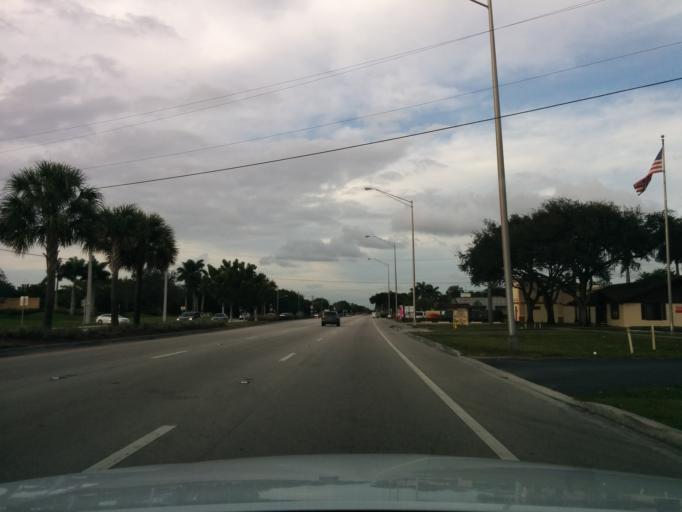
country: US
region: Florida
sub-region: Broward County
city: Davie
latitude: 26.0677
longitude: -80.2522
